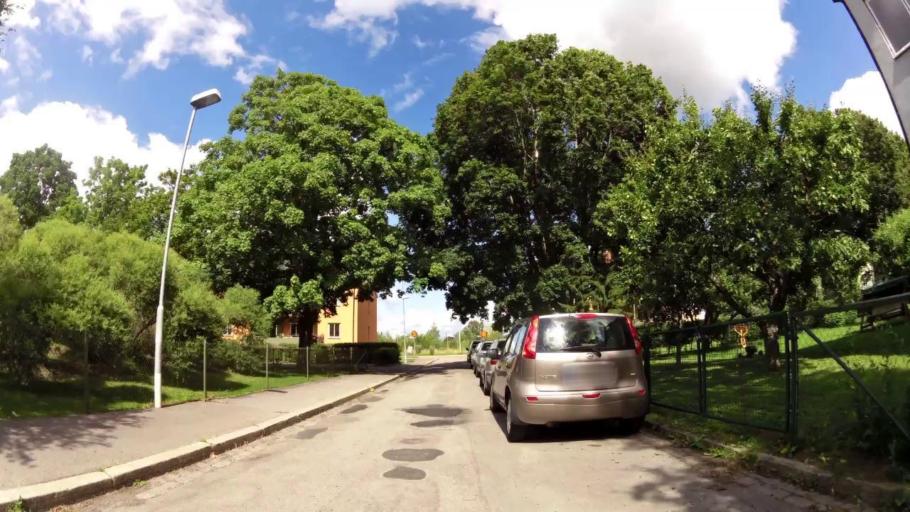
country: SE
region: OEstergoetland
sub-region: Linkopings Kommun
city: Linkoping
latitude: 58.4115
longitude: 15.6417
